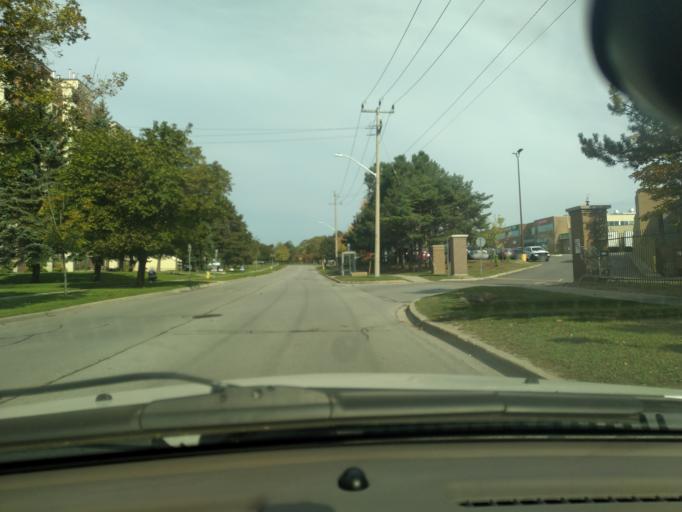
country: CA
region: Ontario
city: Barrie
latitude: 44.4046
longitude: -79.7065
